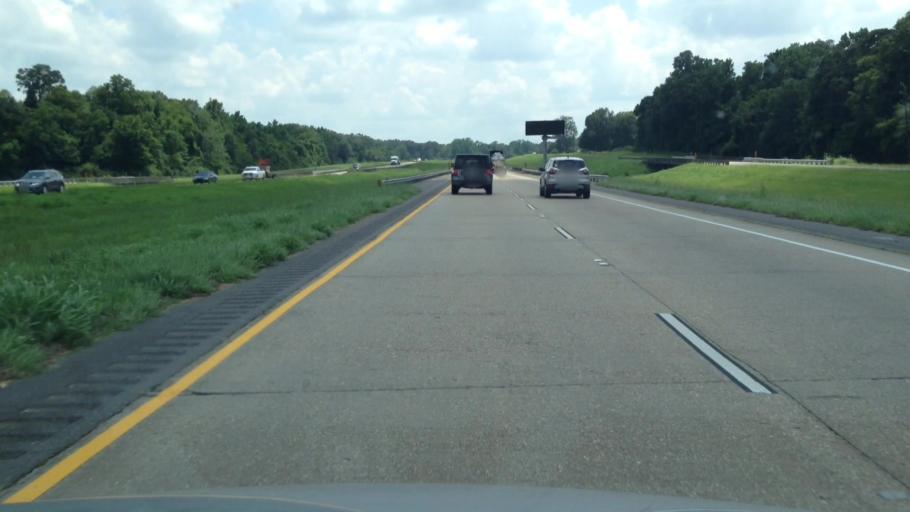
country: US
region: Louisiana
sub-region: Saint Landry Parish
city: Opelousas
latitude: 30.5566
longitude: -92.0525
